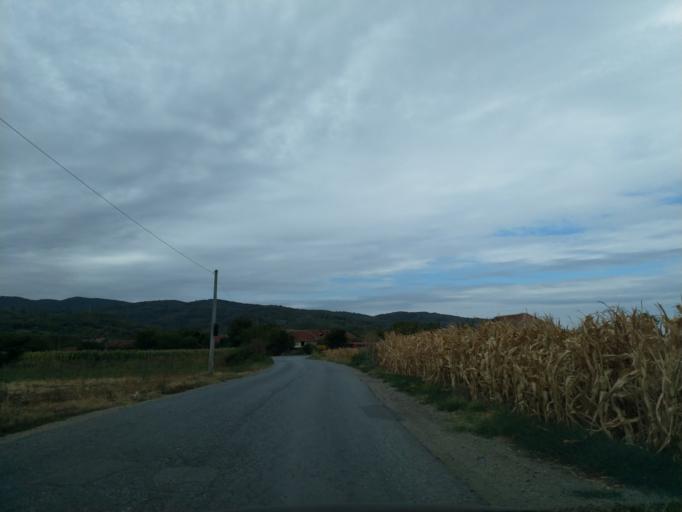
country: RS
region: Central Serbia
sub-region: Pomoravski Okrug
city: Paracin
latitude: 43.8334
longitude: 21.3289
